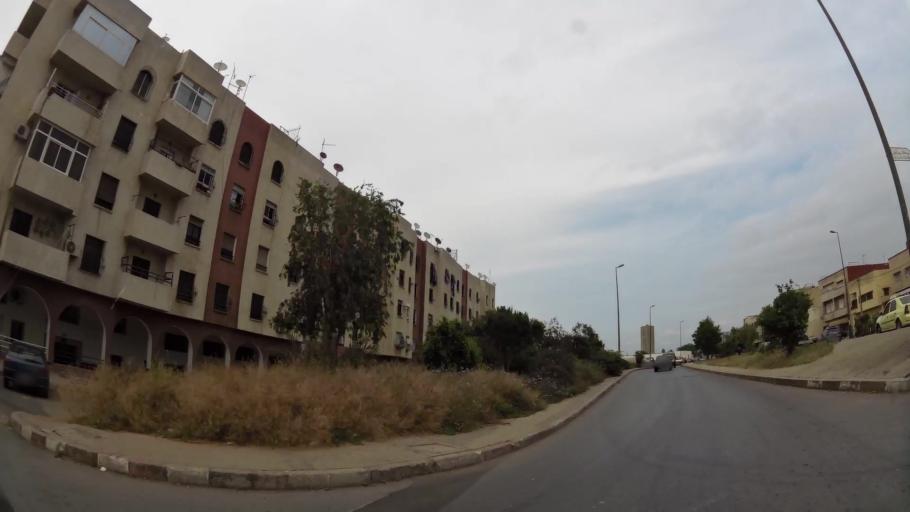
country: MA
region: Rabat-Sale-Zemmour-Zaer
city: Sale
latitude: 34.0338
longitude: -6.8015
